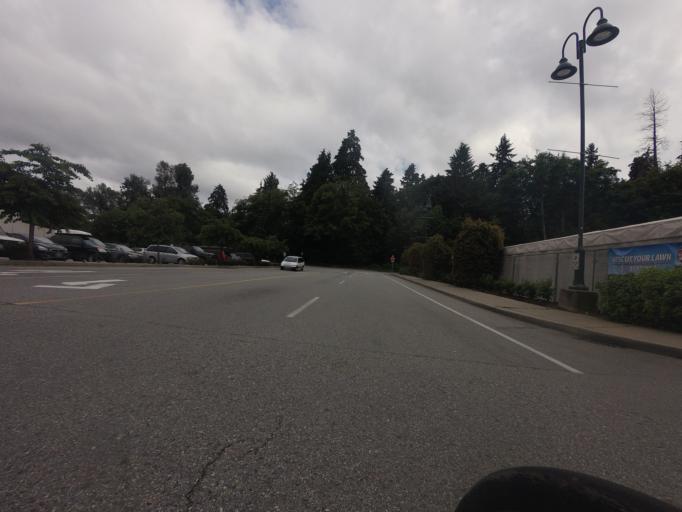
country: CA
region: British Columbia
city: West End
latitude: 49.3247
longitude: -123.1404
